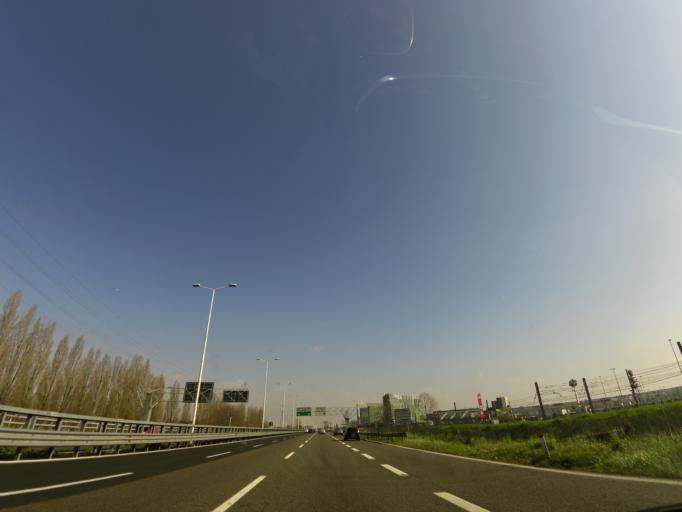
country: IT
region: Lombardy
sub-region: Citta metropolitana di Milano
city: Assago
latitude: 45.4037
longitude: 9.1459
